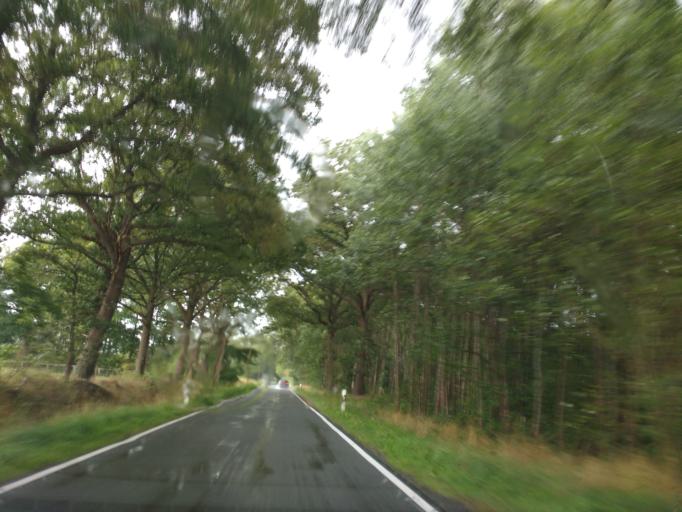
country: DE
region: North Rhine-Westphalia
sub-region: Regierungsbezirk Munster
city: Ostbevern
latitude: 52.1120
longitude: 7.8892
